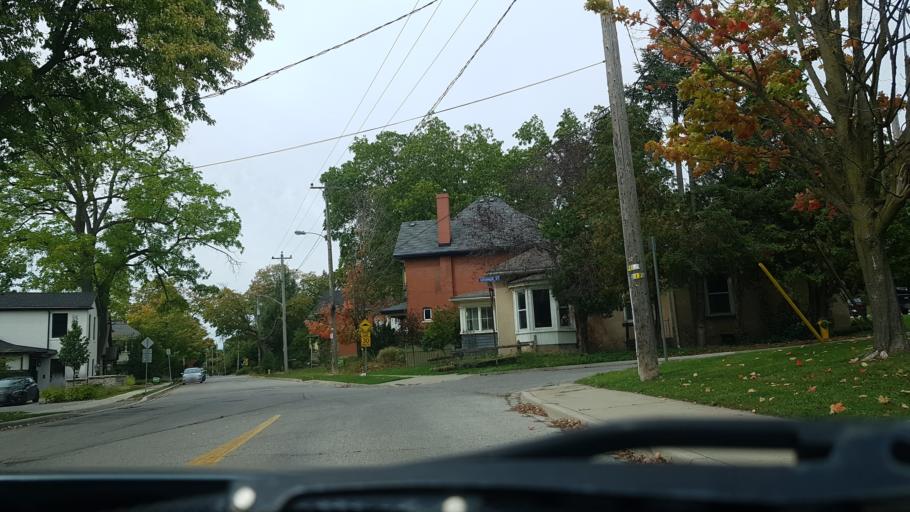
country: CA
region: Ontario
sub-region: Wellington County
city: Guelph
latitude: 43.5490
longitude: -80.2454
